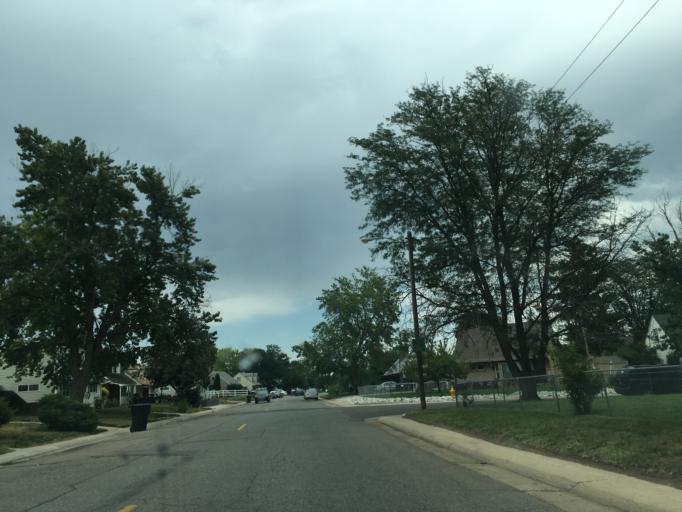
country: US
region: Colorado
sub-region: Arapahoe County
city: Sheridan
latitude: 39.6731
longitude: -105.0285
